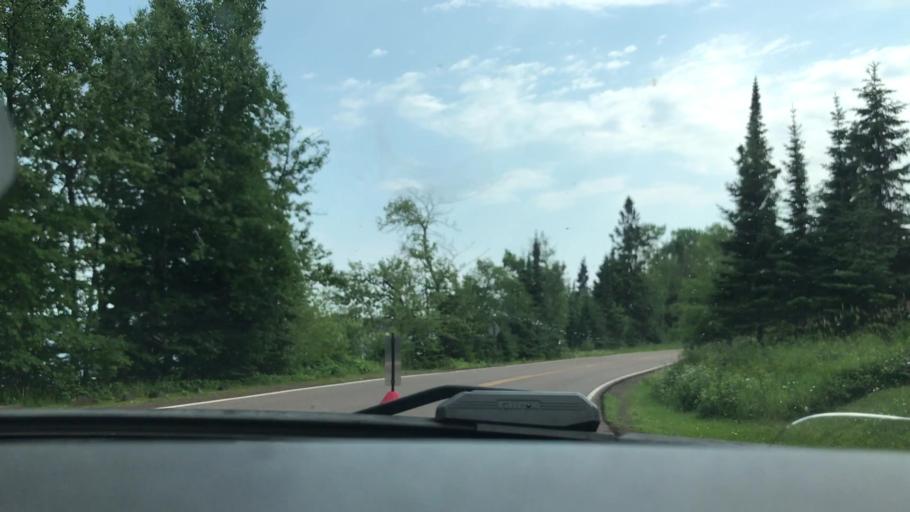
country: CA
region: Ontario
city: Neebing
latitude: 47.9612
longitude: -89.6859
